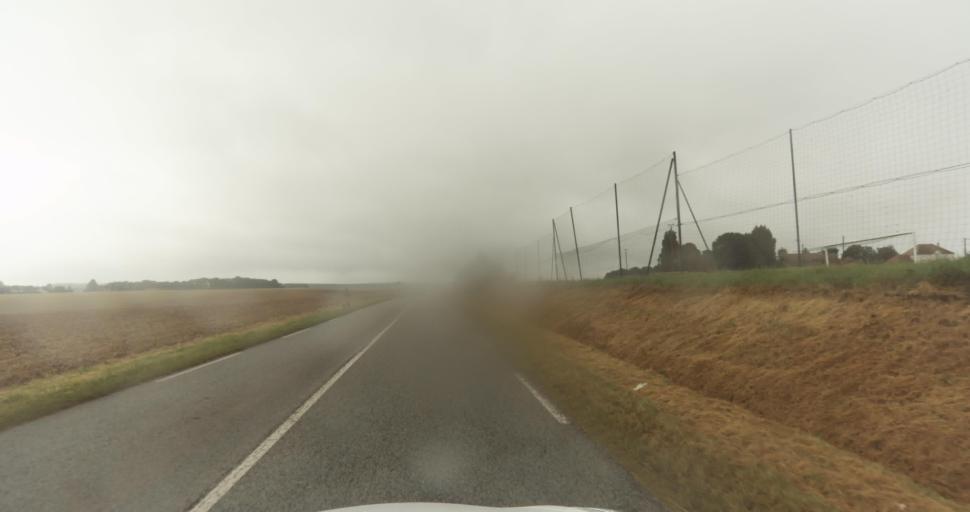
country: FR
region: Haute-Normandie
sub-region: Departement de l'Eure
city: Heudreville-sur-Eure
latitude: 49.1111
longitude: 1.1737
